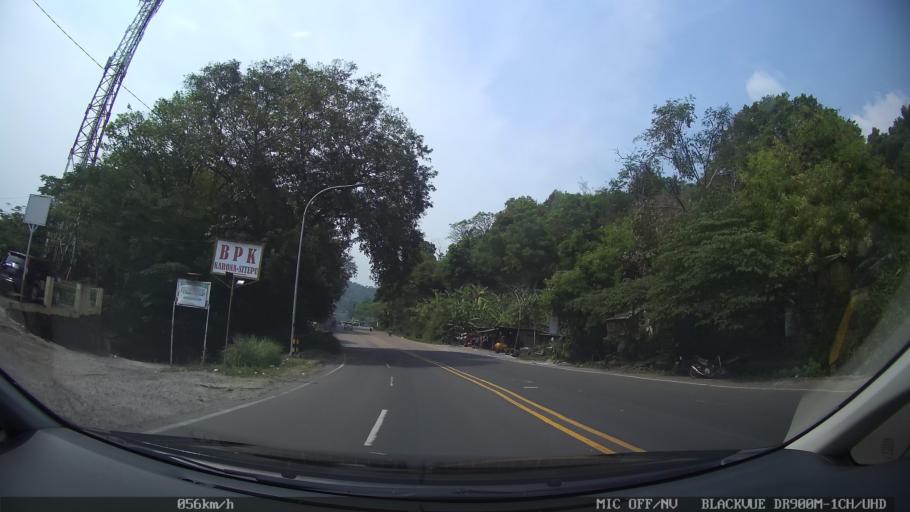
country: ID
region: Banten
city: Curug
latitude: -5.9480
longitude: 106.0036
